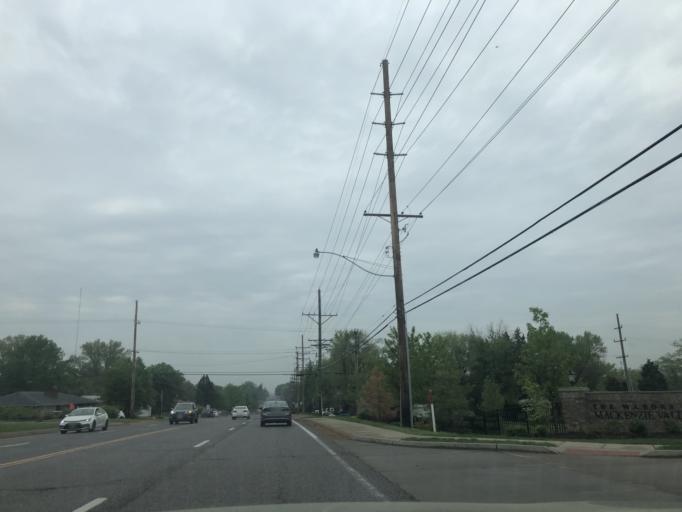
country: US
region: Missouri
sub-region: Saint Louis County
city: Affton
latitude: 38.5595
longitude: -90.3218
